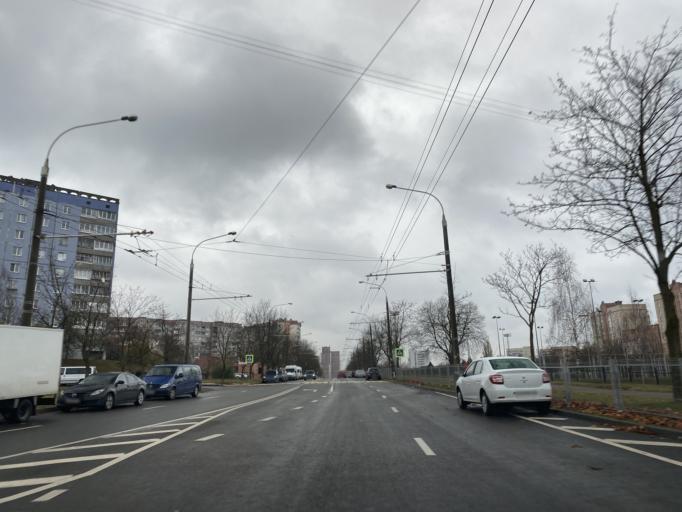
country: BY
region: Minsk
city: Bal'shavik
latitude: 53.9568
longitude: 27.6080
